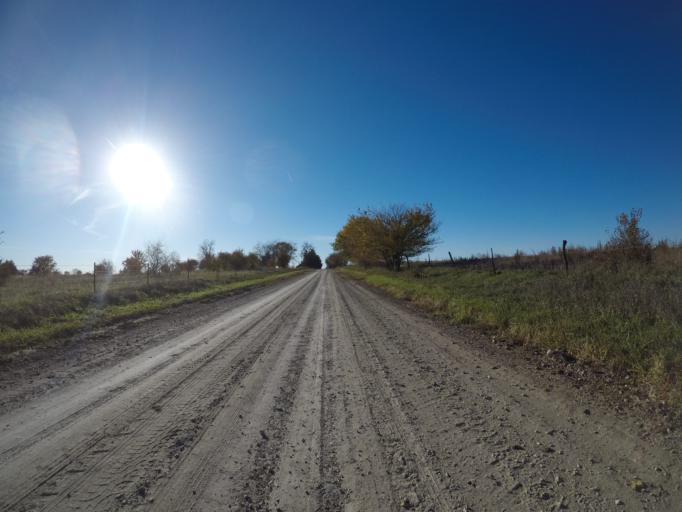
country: US
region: Kansas
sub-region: Riley County
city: Ogden
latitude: 39.2620
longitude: -96.7583
